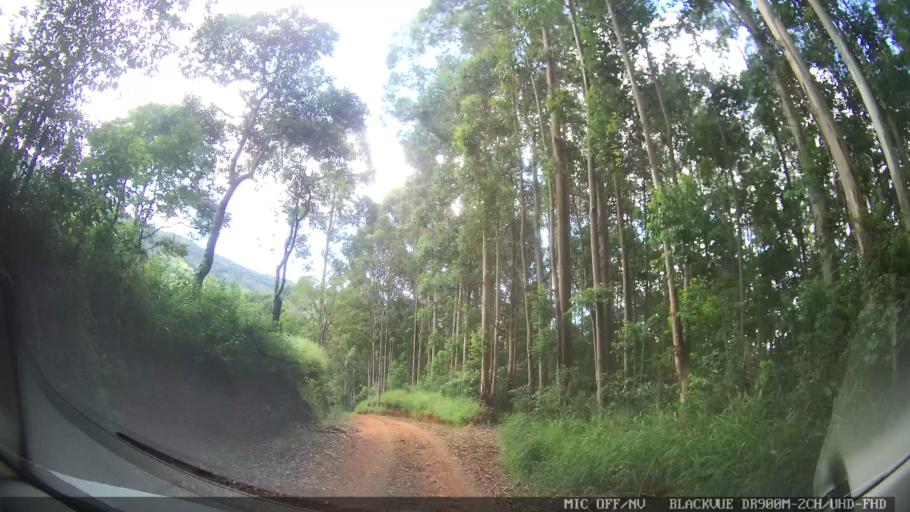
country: BR
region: Minas Gerais
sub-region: Extrema
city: Extrema
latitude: -22.8796
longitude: -46.2930
